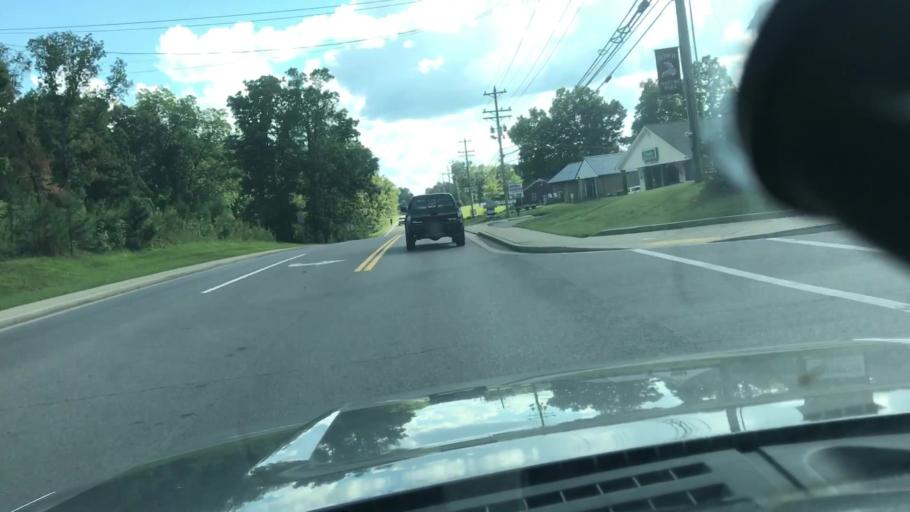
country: US
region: Tennessee
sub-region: Williamson County
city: Fairview
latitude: 35.9694
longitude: -87.1310
